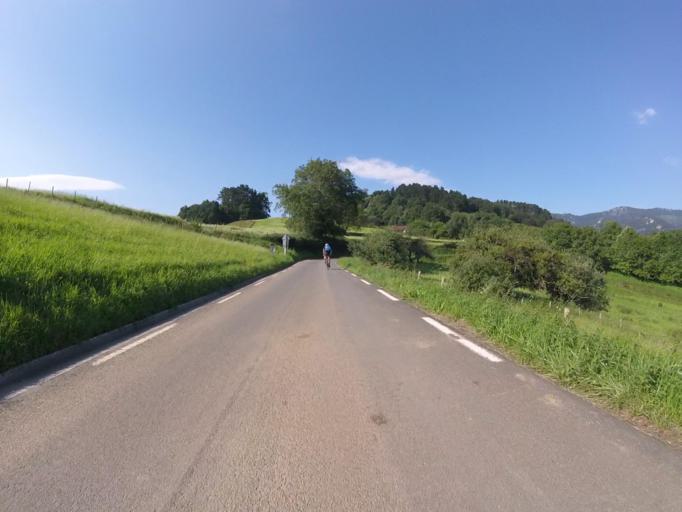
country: ES
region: Basque Country
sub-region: Provincia de Guipuzcoa
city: Larraul
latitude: 43.1805
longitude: -2.0886
